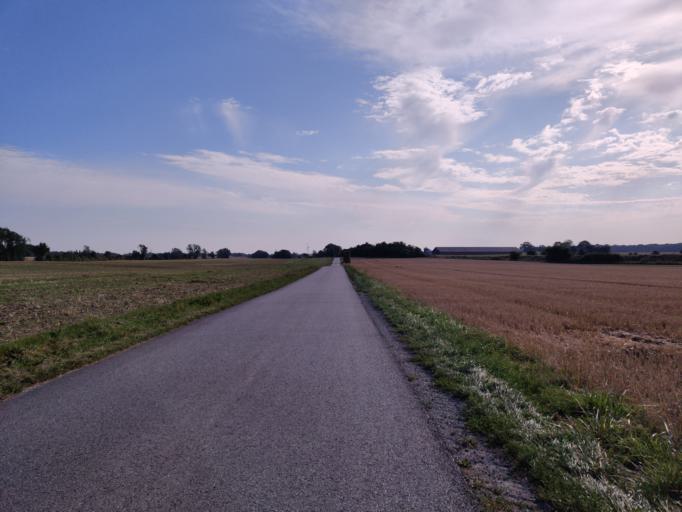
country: DK
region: Zealand
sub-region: Guldborgsund Kommune
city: Nykobing Falster
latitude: 54.6968
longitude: 11.9054
